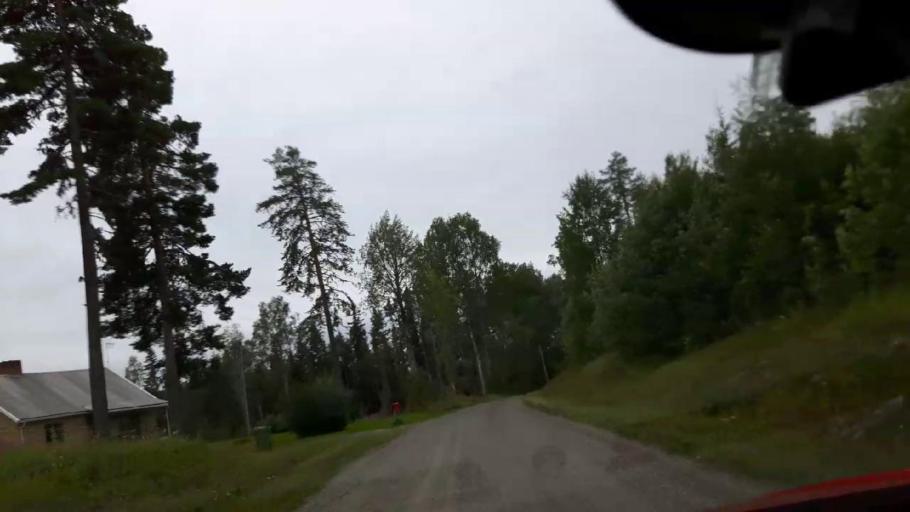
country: SE
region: Vaesternorrland
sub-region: Ange Kommun
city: Ange
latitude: 62.8546
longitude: 15.9069
